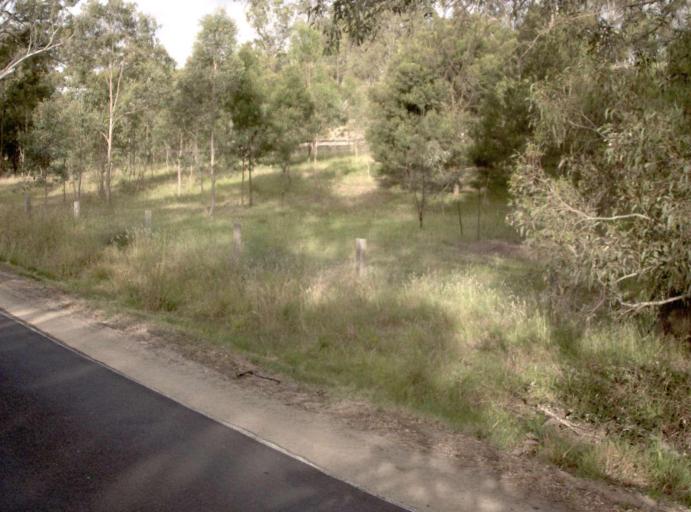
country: AU
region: Victoria
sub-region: Wellington
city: Sale
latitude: -37.9219
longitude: 146.9979
